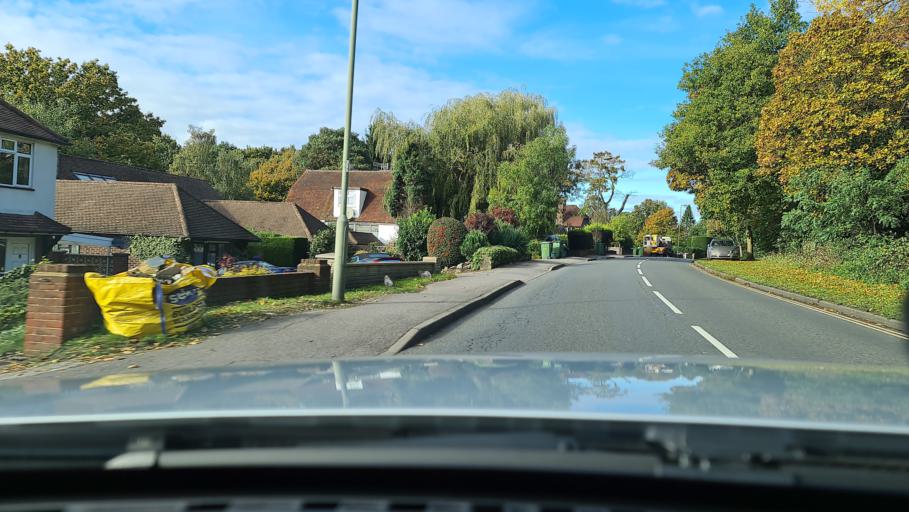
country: GB
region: England
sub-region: Surrey
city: Byfleet
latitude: 51.3427
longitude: -0.4633
